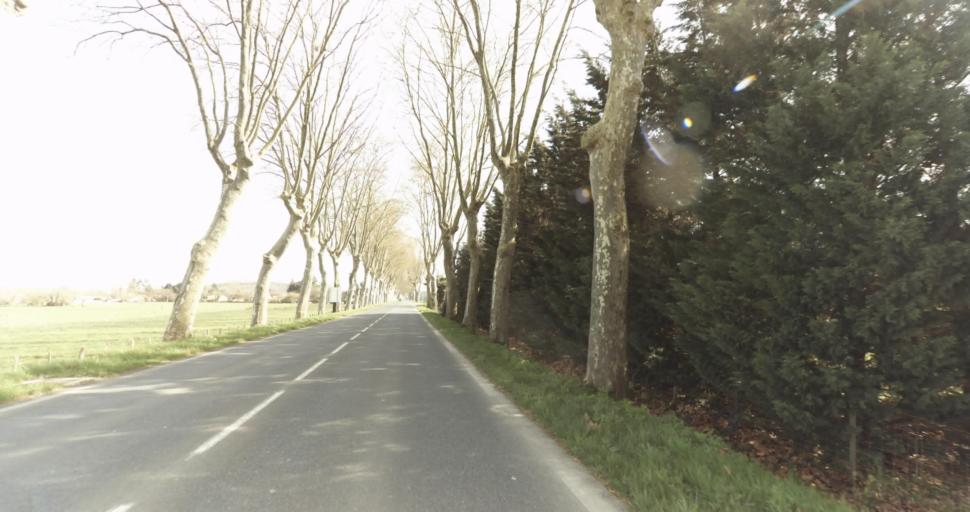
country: FR
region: Midi-Pyrenees
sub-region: Departement du Tarn
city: Saint-Sulpice-la-Pointe
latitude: 43.7756
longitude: 1.6646
